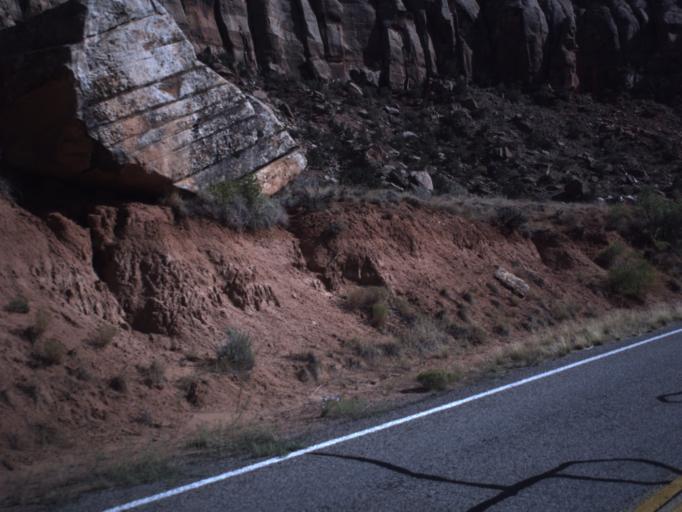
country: US
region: Utah
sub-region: San Juan County
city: Monticello
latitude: 38.0442
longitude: -109.5517
